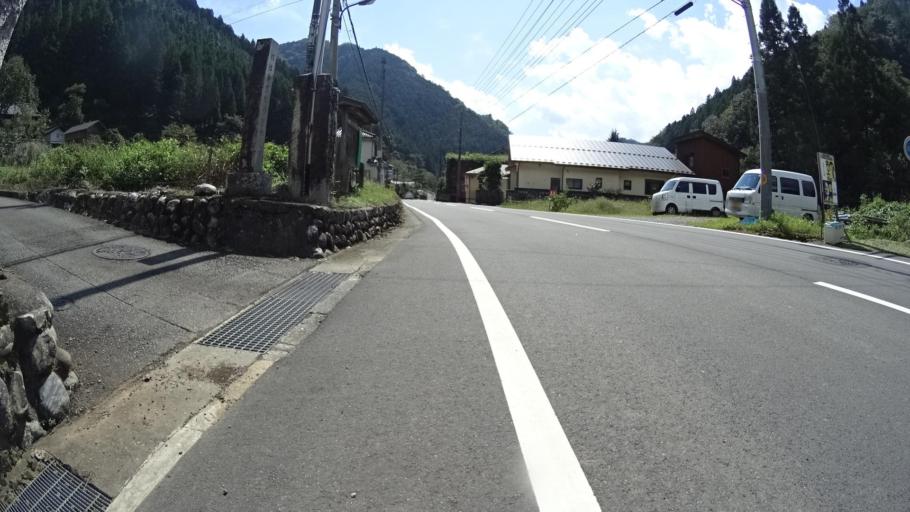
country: JP
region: Tokyo
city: Itsukaichi
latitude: 35.7380
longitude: 139.1435
